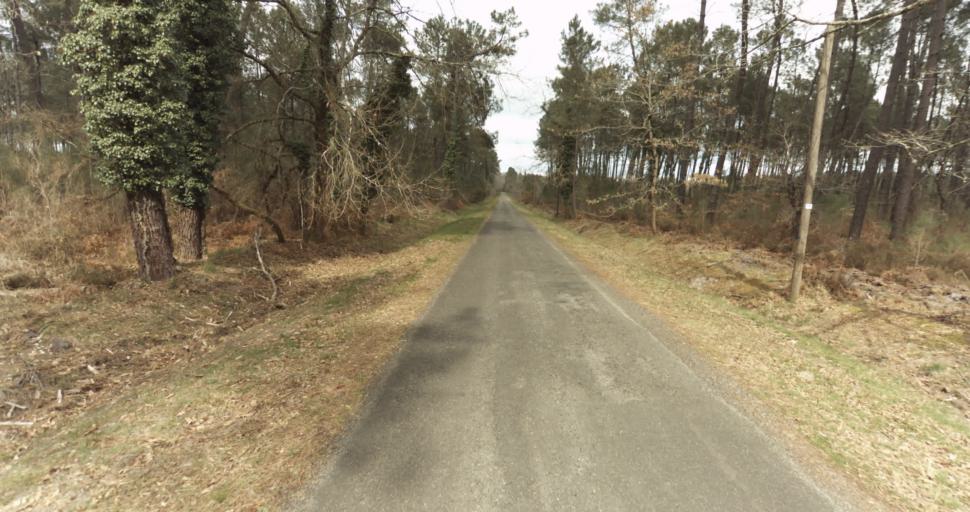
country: FR
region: Aquitaine
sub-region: Departement des Landes
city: Roquefort
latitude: 44.0545
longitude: -0.3779
